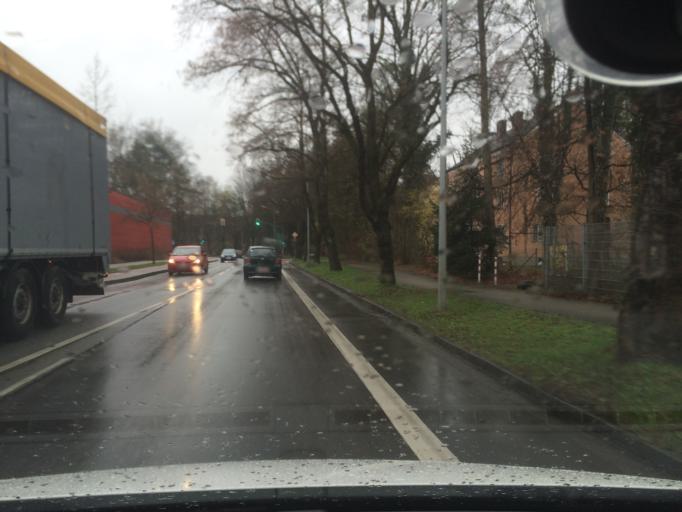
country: DE
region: Bavaria
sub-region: Upper Bavaria
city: Rosenheim
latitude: 47.8653
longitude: 12.1098
